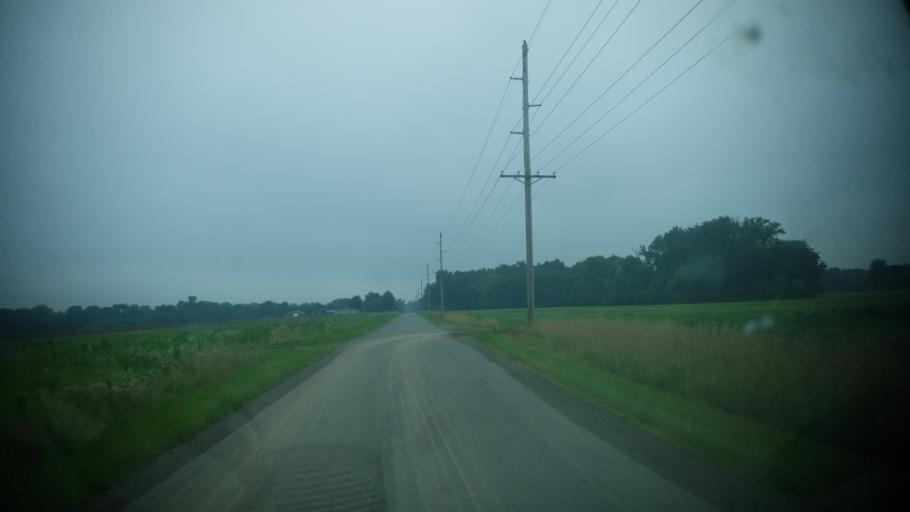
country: US
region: Illinois
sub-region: Clay County
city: Flora
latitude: 38.5515
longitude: -88.4019
